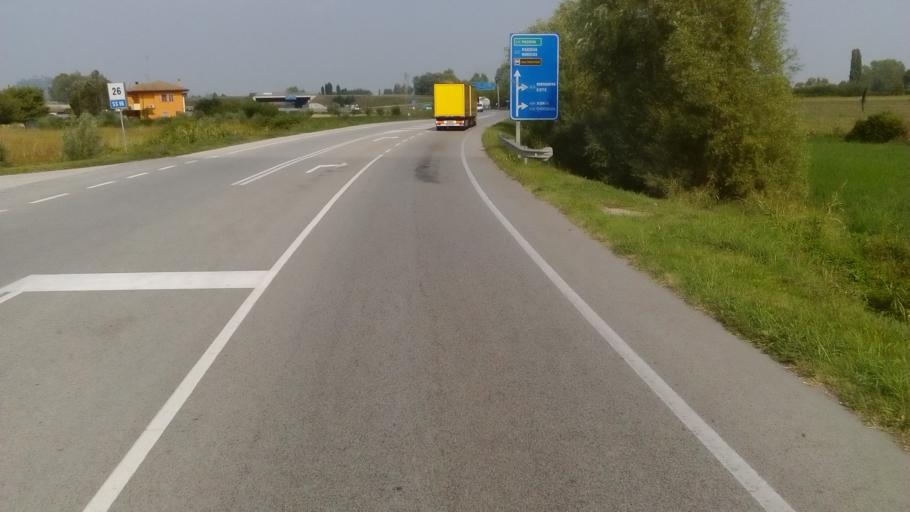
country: IT
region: Veneto
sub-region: Provincia di Padova
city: Monselice
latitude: 45.2046
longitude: 11.7559
